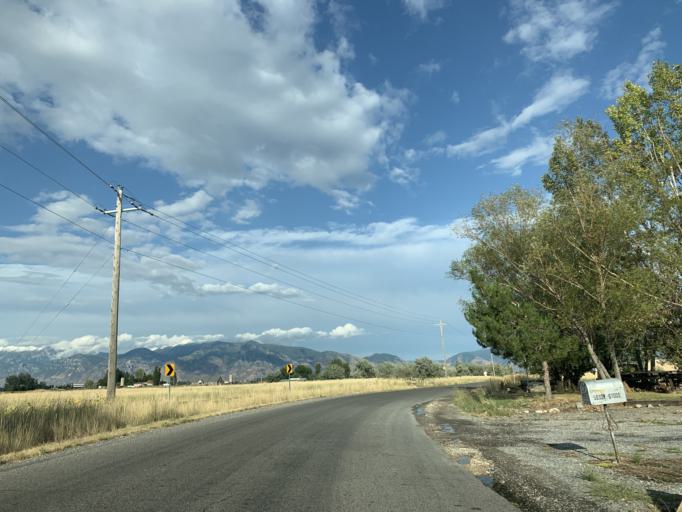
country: US
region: Utah
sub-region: Utah County
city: Benjamin
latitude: 40.1163
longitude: -111.7748
